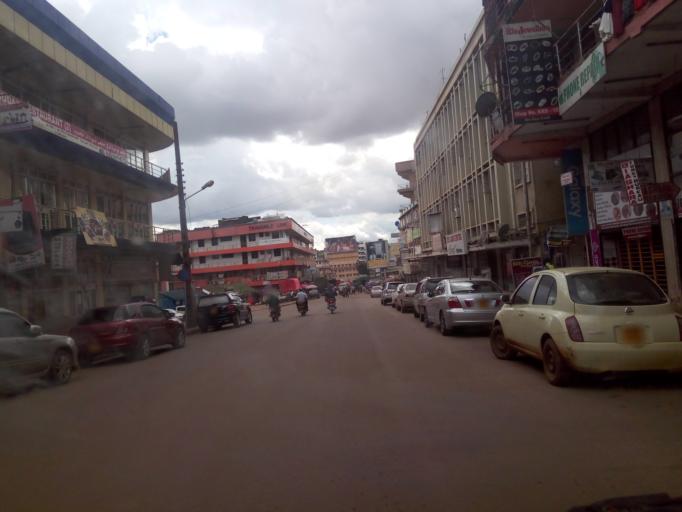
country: UG
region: Central Region
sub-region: Kampala District
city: Kampala
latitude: 0.3160
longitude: 32.5751
